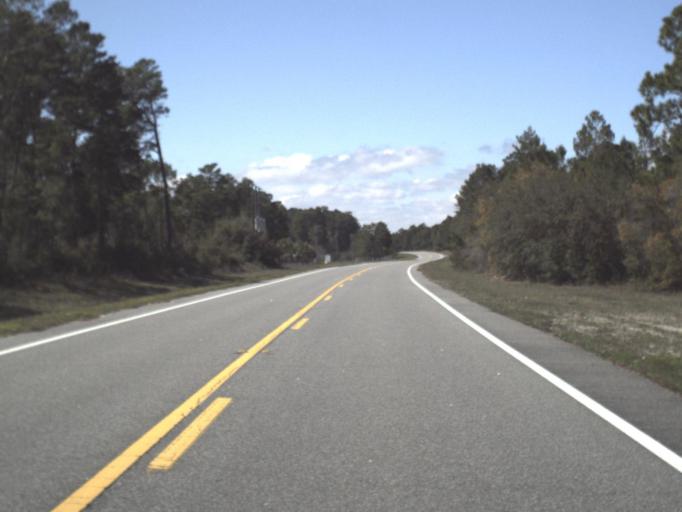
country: US
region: Florida
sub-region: Franklin County
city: Carrabelle
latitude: 29.9293
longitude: -84.4351
